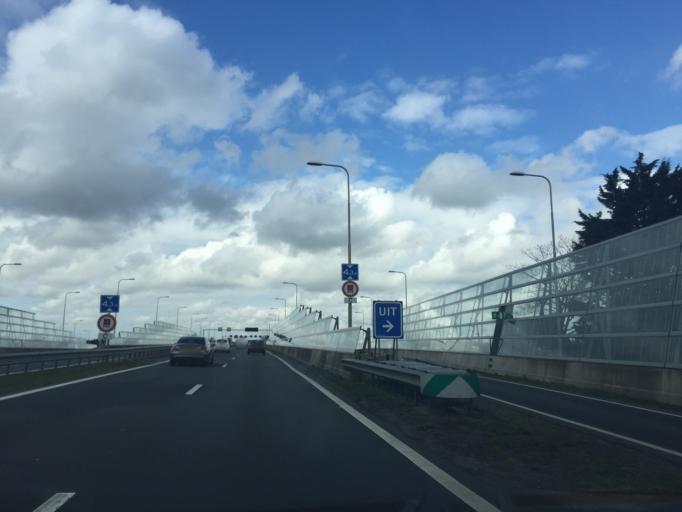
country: NL
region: North Holland
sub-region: Gemeente Aalsmeer
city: Aalsmeer
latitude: 52.2684
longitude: 4.7892
